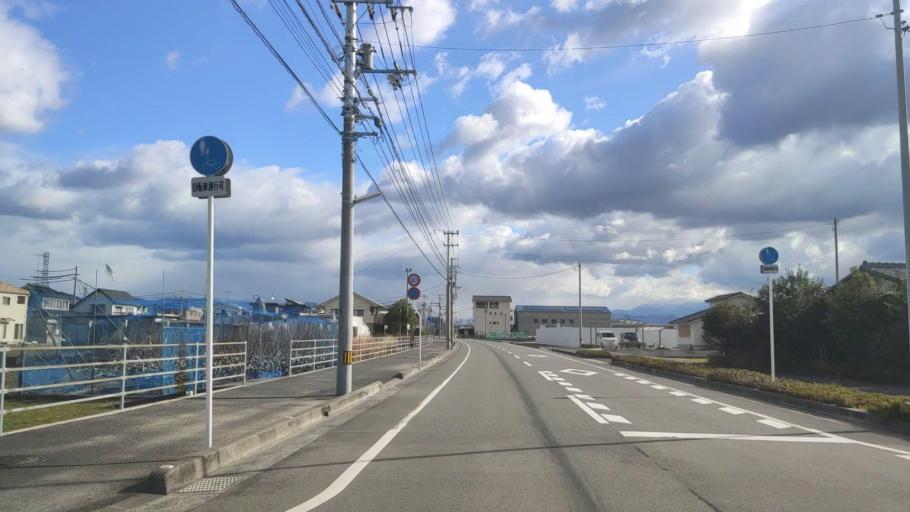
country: JP
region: Ehime
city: Masaki-cho
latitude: 33.8175
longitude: 132.7158
